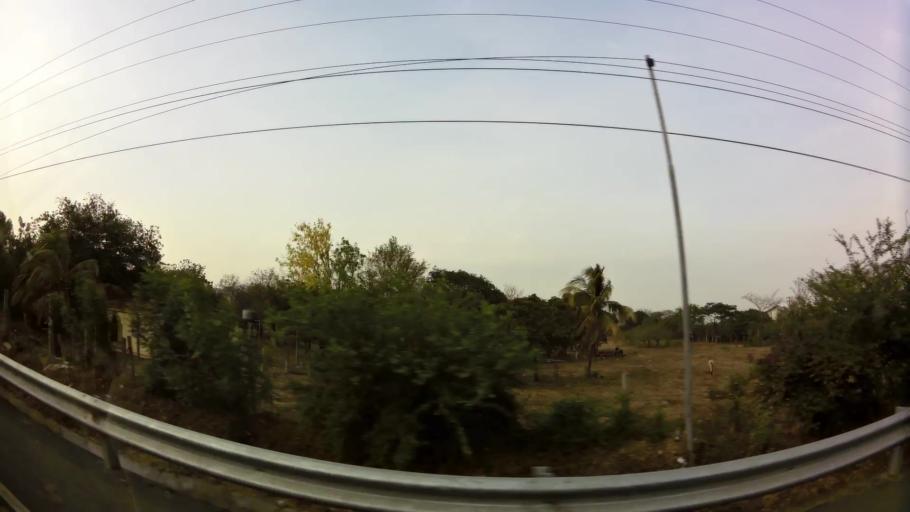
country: NI
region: Managua
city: Ciudad Sandino
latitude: 12.1783
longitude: -86.3527
